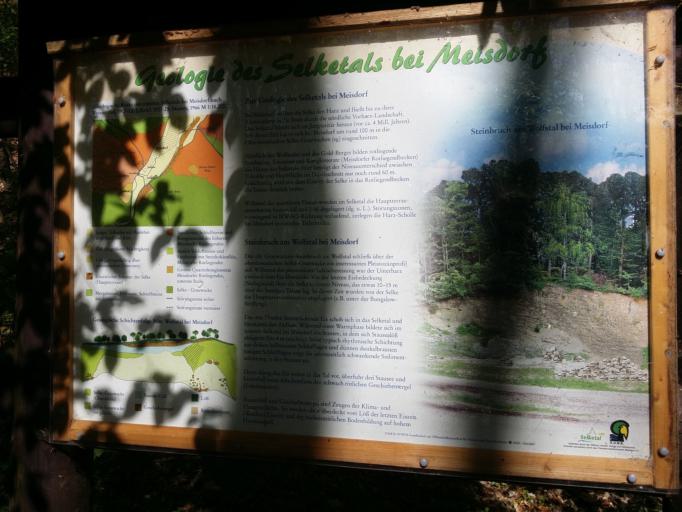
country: DE
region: Saxony-Anhalt
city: Ballenstedt
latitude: 51.6973
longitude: 11.2832
